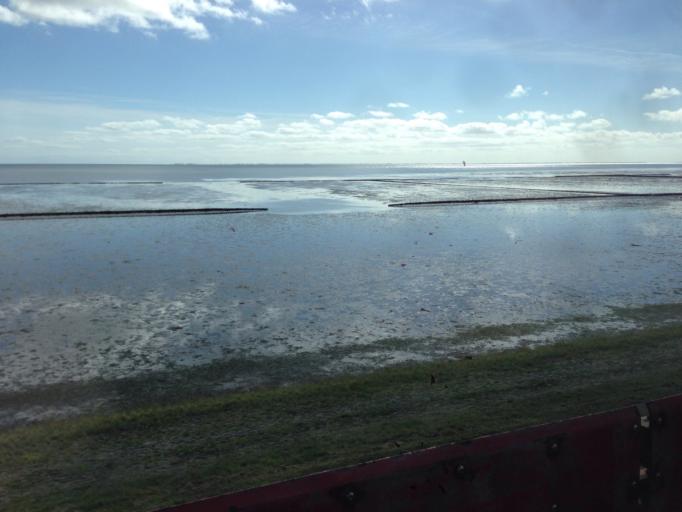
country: DE
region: Schleswig-Holstein
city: Sylt-Ost
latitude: 54.8779
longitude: 8.4941
